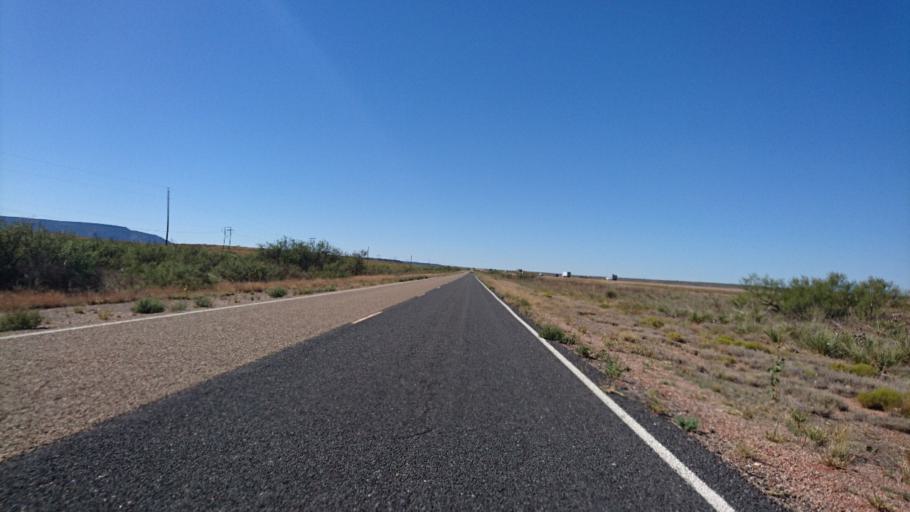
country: US
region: New Mexico
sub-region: Quay County
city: Tucumcari
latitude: 35.0890
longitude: -104.0864
